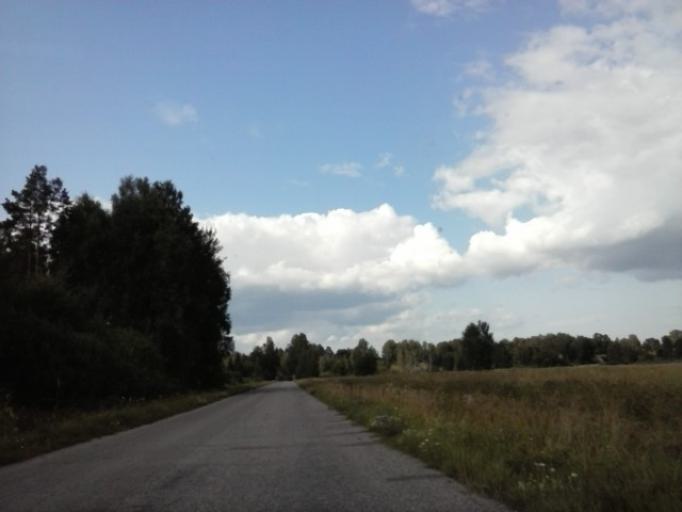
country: EE
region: Vorumaa
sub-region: Voru linn
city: Voru
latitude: 57.8265
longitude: 27.1288
